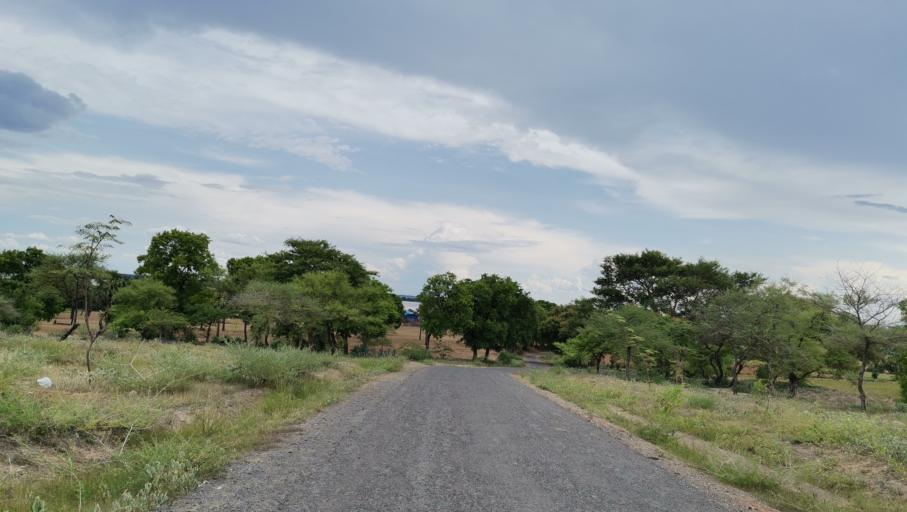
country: MM
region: Mandalay
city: Myingyan
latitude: 21.8172
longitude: 95.3977
